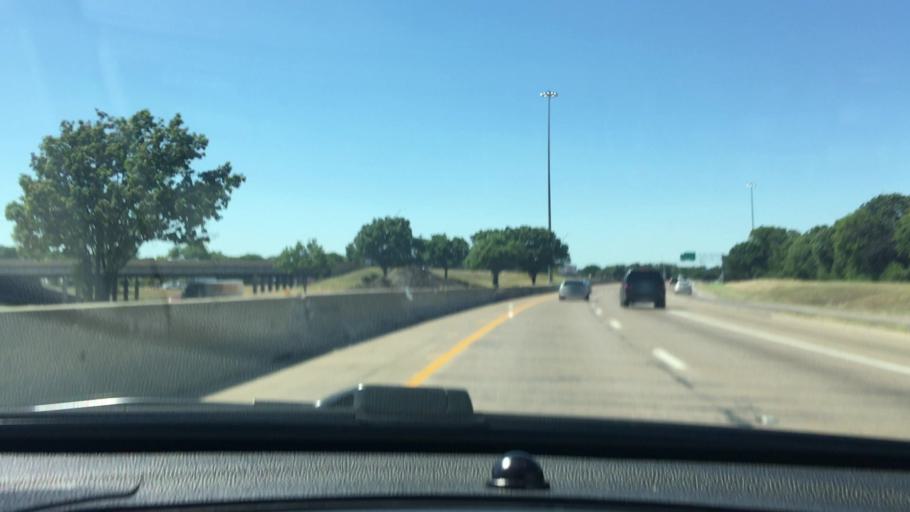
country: US
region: Texas
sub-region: Dallas County
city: Cockrell Hill
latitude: 32.7072
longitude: -96.8285
